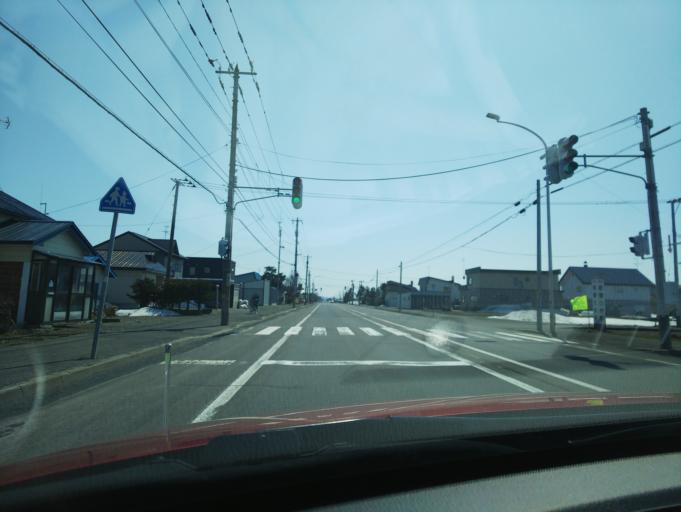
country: JP
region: Hokkaido
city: Nayoro
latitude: 44.2374
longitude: 142.3949
